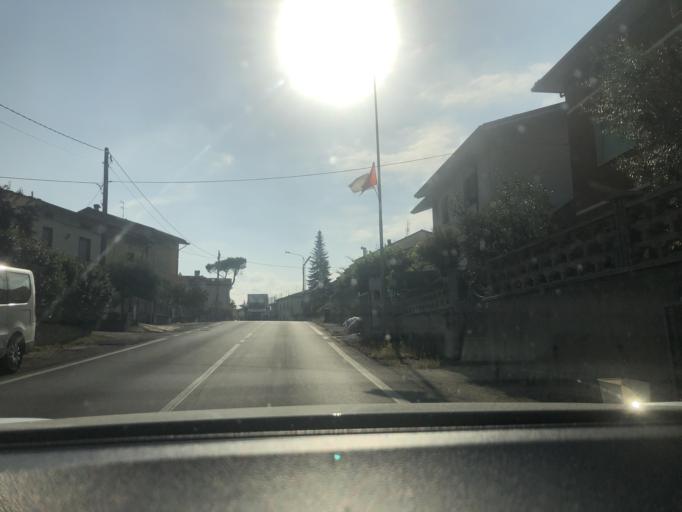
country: IT
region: Tuscany
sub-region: Province of Florence
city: Lazzeretto
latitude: 43.8031
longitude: 10.8497
